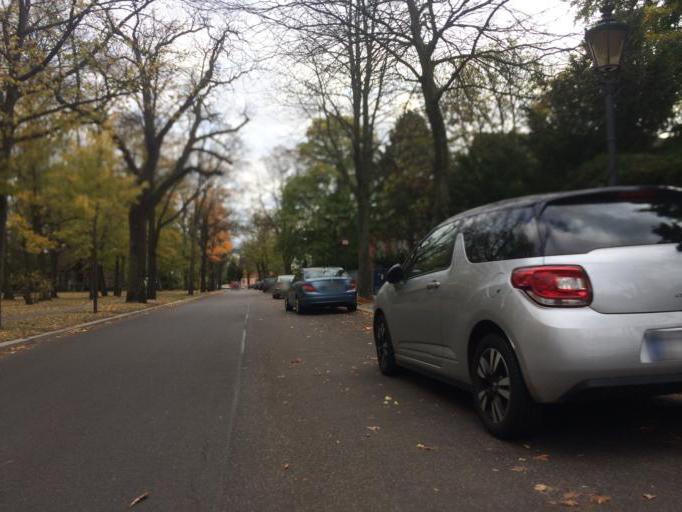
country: DE
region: Berlin
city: Wittenau
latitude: 52.5927
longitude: 13.3235
